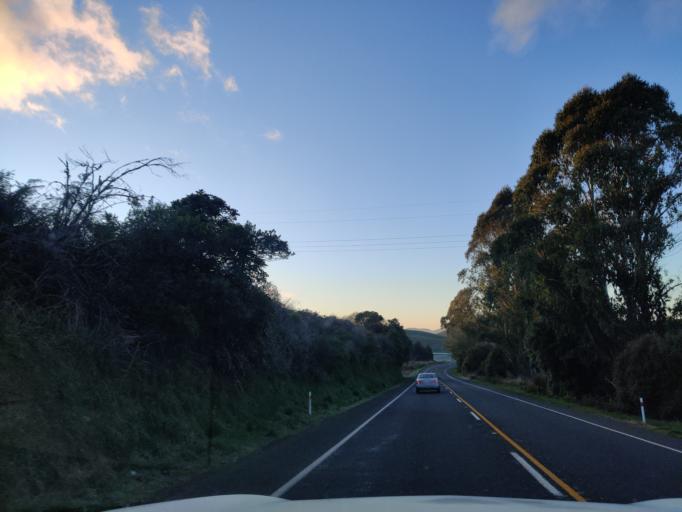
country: NZ
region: Waikato
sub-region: Taupo District
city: Taupo
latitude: -38.6276
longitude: 176.0412
